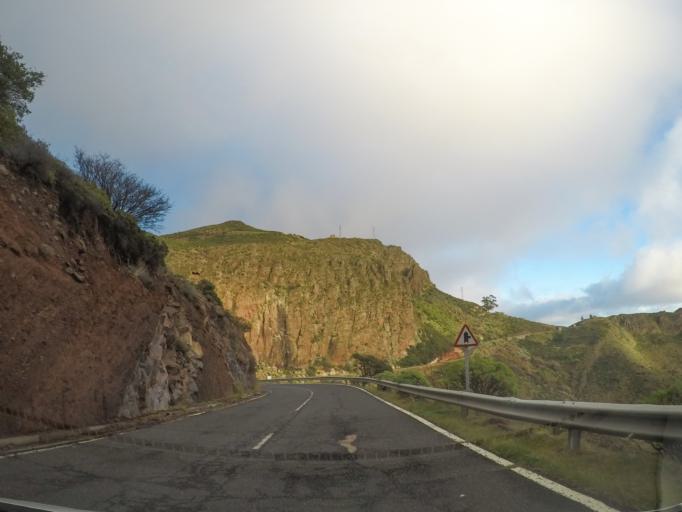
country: ES
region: Canary Islands
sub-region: Provincia de Santa Cruz de Tenerife
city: Alajero
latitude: 28.0889
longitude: -17.2541
